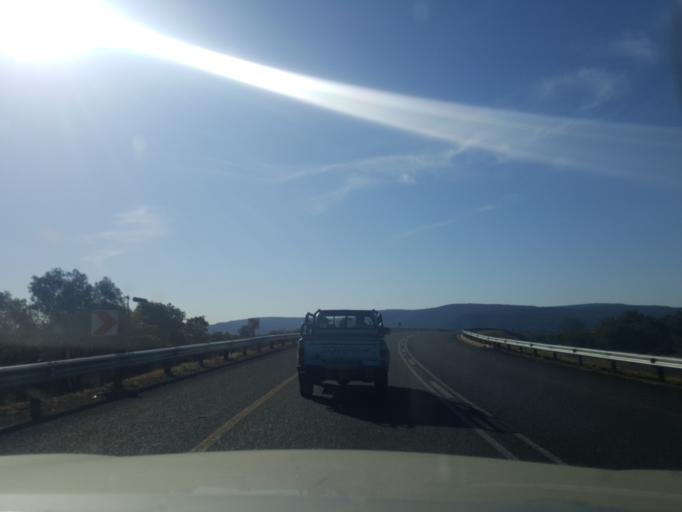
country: ZA
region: North-West
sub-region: Ngaka Modiri Molema District Municipality
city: Zeerust
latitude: -25.5329
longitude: 26.1915
